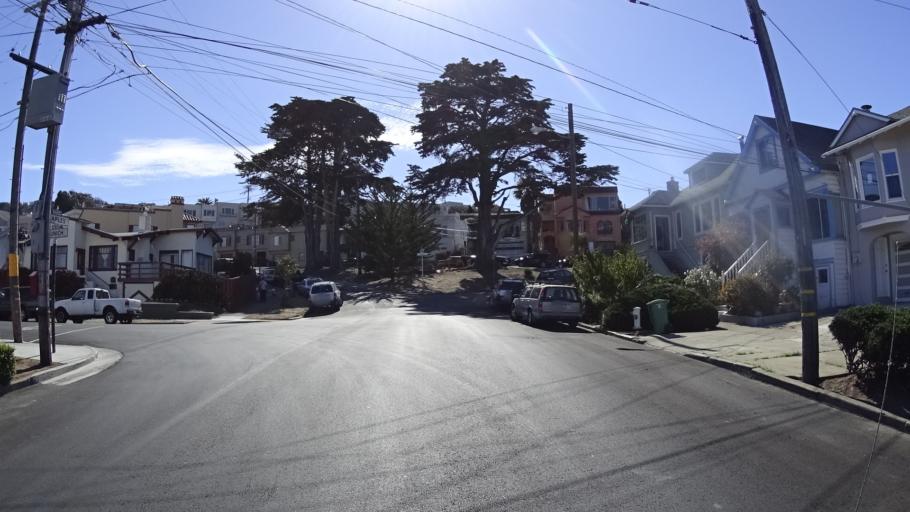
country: US
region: California
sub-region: San Mateo County
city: Daly City
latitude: 37.7113
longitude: -122.4382
